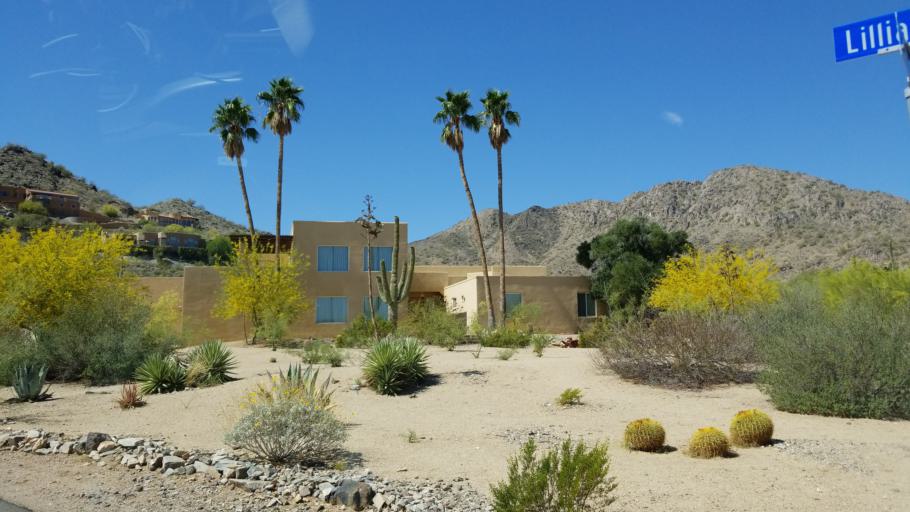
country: US
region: Arizona
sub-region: Maricopa County
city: Paradise Valley
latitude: 33.5609
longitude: -111.9786
